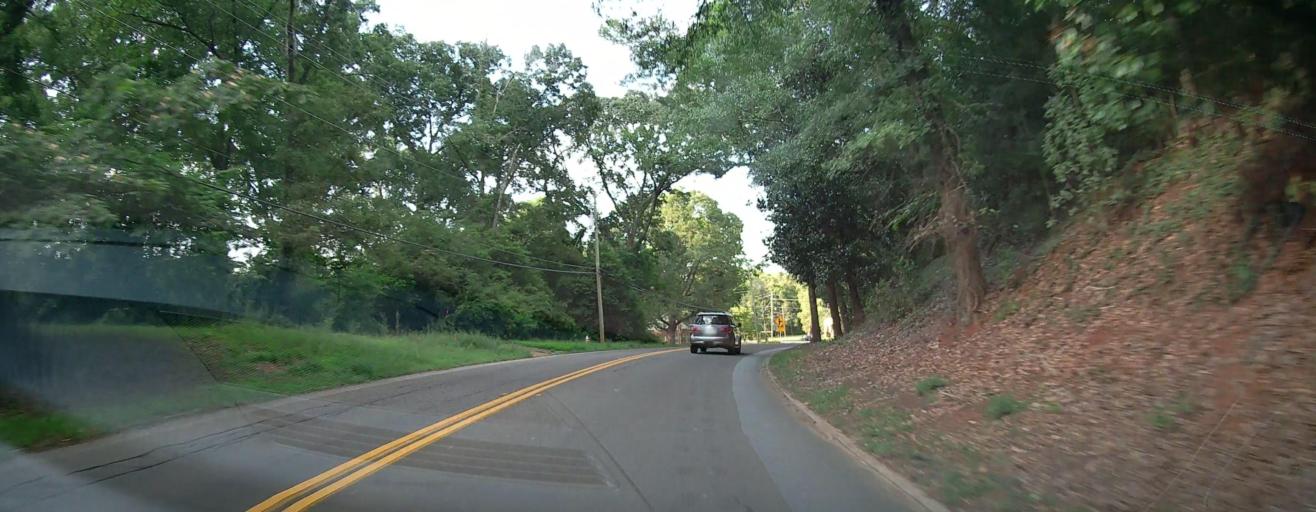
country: US
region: Georgia
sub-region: Monroe County
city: Forsyth
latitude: 33.0281
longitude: -83.9397
